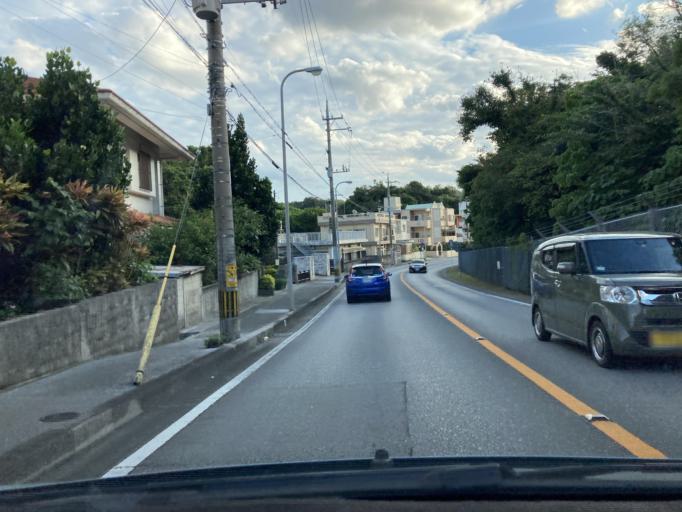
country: JP
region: Okinawa
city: Chatan
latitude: 26.3148
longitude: 127.7673
